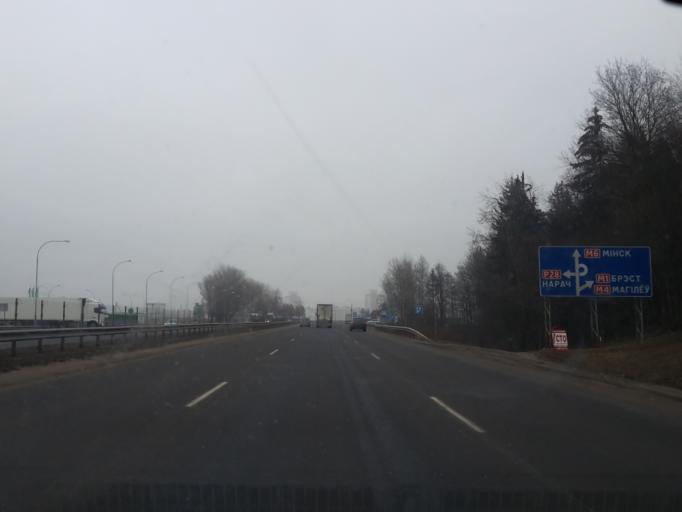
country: BY
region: Minsk
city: Zhdanovichy
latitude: 53.9106
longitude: 27.3967
